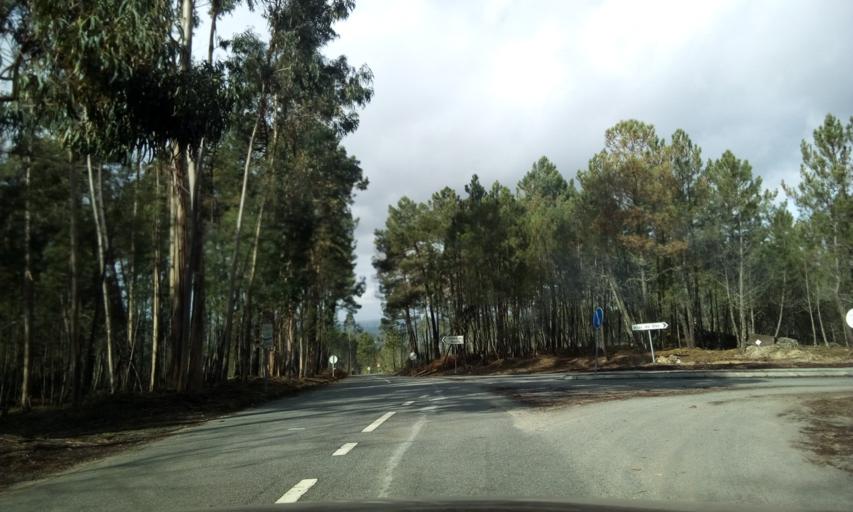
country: PT
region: Guarda
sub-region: Fornos de Algodres
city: Fornos de Algodres
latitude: 40.6620
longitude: -7.6422
